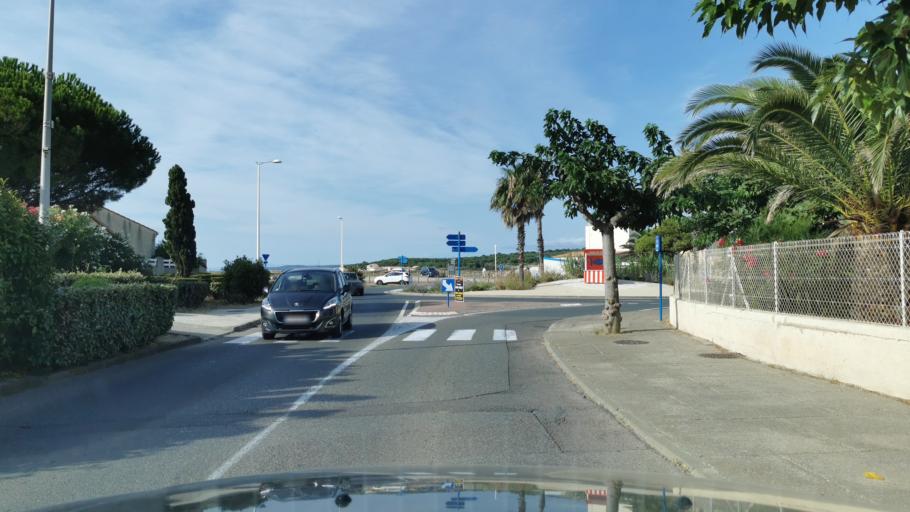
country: FR
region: Languedoc-Roussillon
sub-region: Departement de l'Aude
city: Gruissan
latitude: 43.1038
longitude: 3.0909
